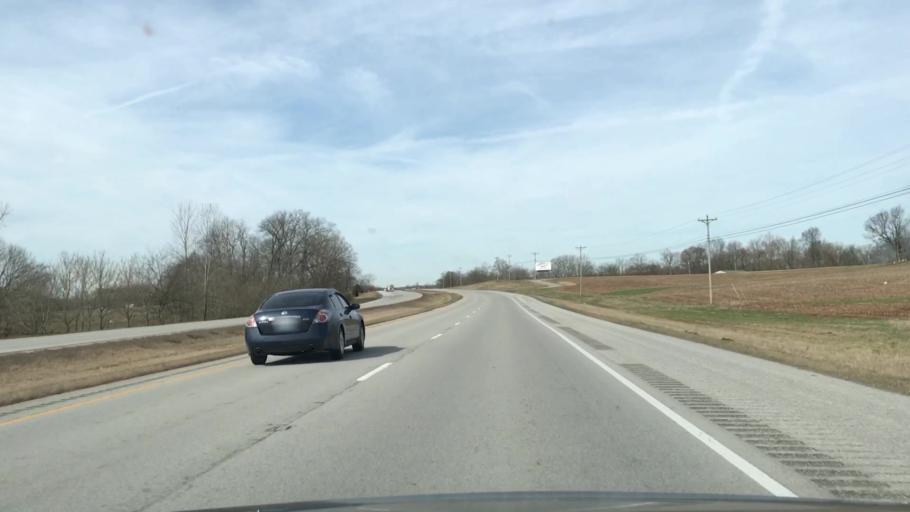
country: US
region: Kentucky
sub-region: Christian County
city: Hopkinsville
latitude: 36.8812
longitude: -87.5988
